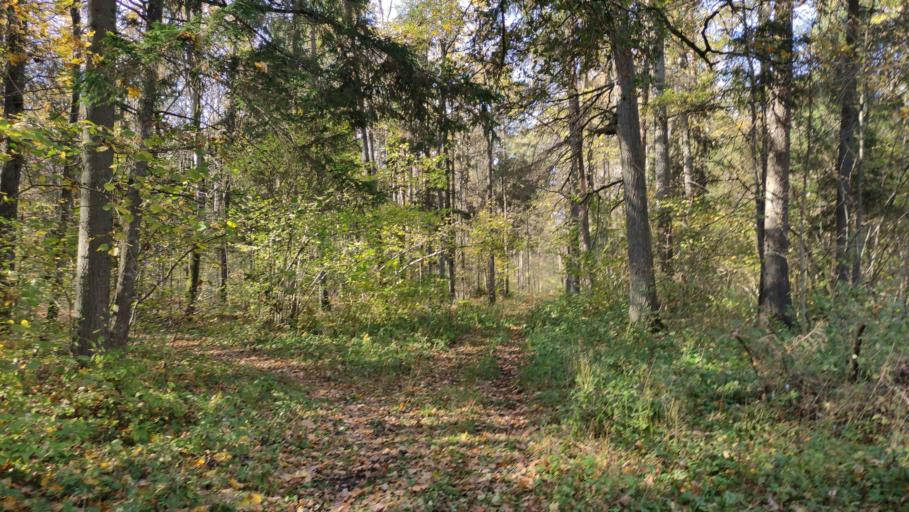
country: LT
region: Alytaus apskritis
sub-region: Alytus
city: Alytus
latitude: 54.3817
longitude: 24.0825
